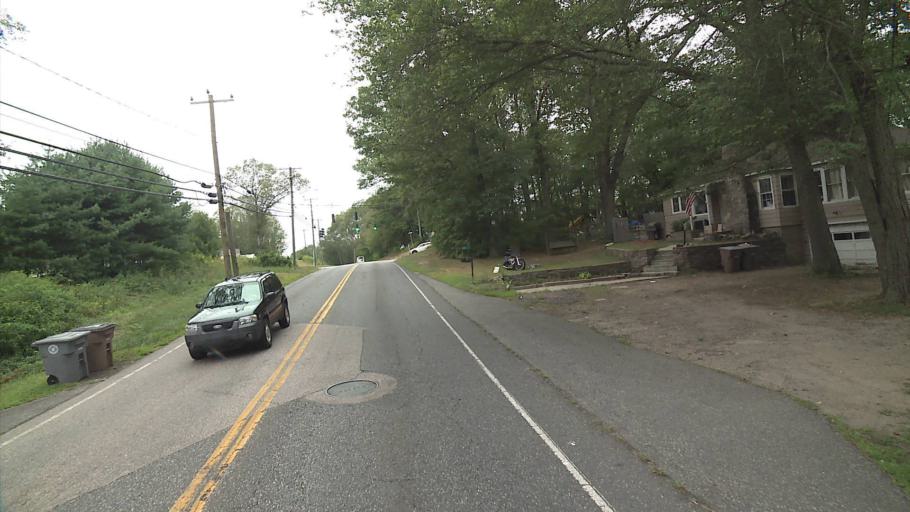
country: US
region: Connecticut
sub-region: New London County
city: Niantic
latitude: 41.3191
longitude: -72.2295
